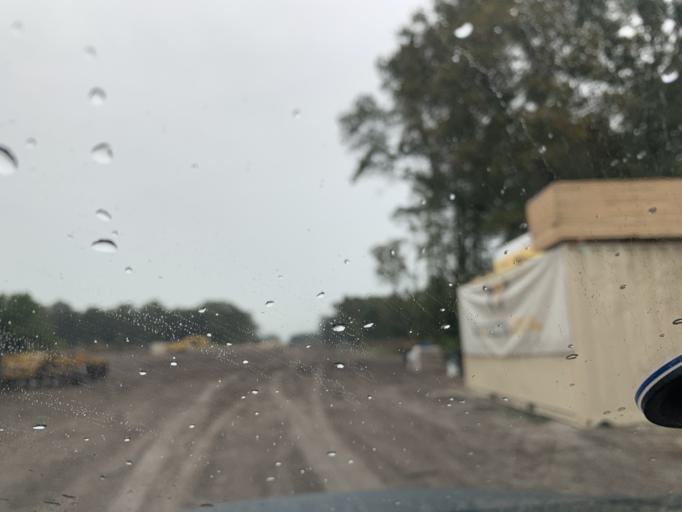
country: US
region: Florida
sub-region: Hernando County
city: Masaryktown
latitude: 28.4518
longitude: -82.4586
